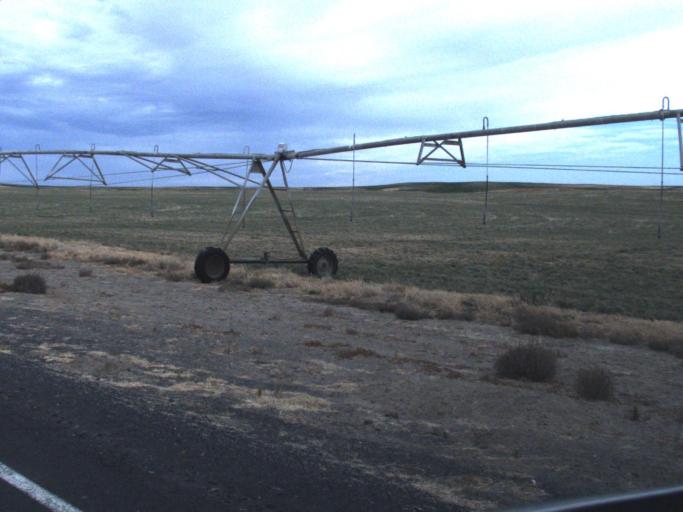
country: US
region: Washington
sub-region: Okanogan County
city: Coulee Dam
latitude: 47.4767
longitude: -118.7848
